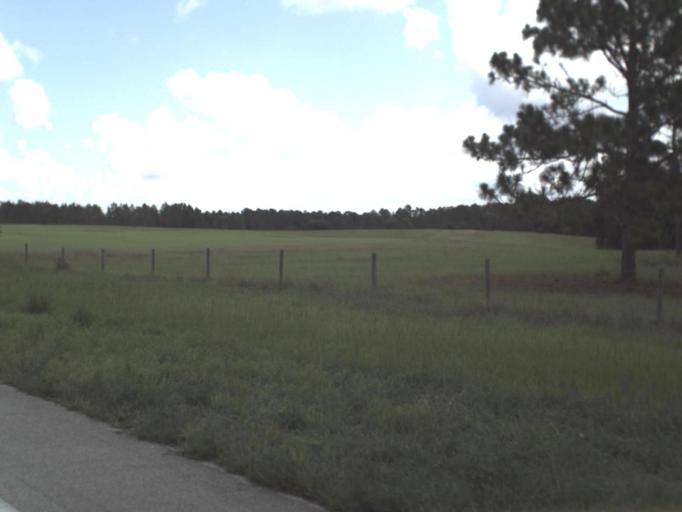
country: US
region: Florida
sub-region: Putnam County
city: Palatka
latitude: 29.5320
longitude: -81.6426
